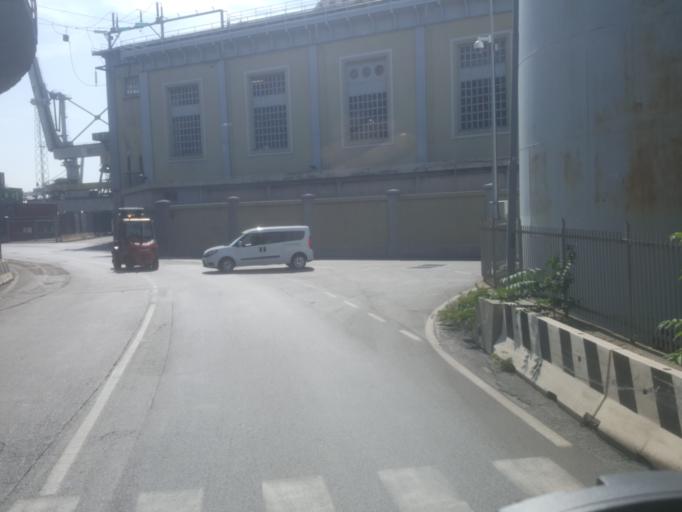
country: IT
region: Liguria
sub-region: Provincia di Genova
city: San Teodoro
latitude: 44.4041
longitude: 8.9037
